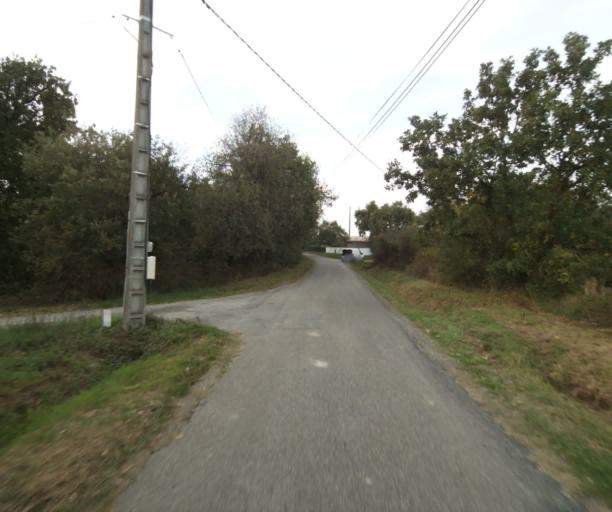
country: FR
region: Midi-Pyrenees
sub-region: Departement du Tarn-et-Garonne
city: Pompignan
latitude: 43.8256
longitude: 1.3139
